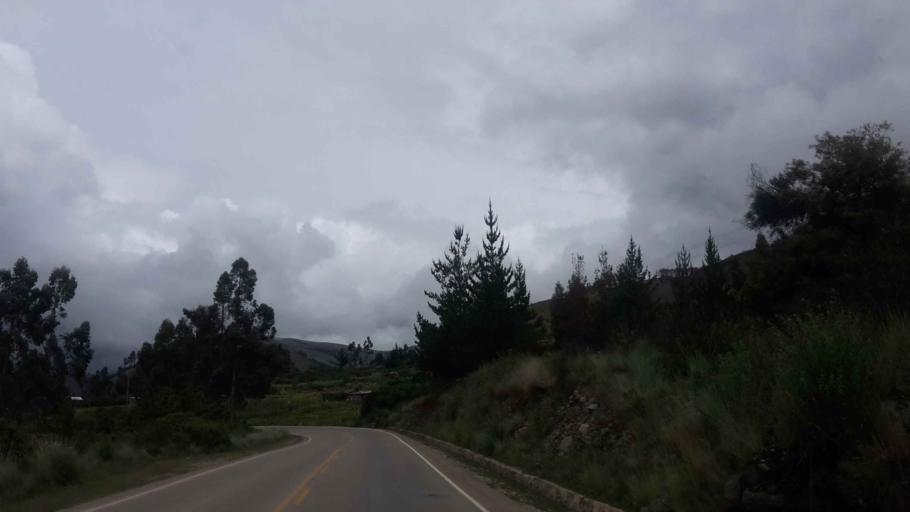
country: BO
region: Cochabamba
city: Arani
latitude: -17.4767
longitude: -65.5087
